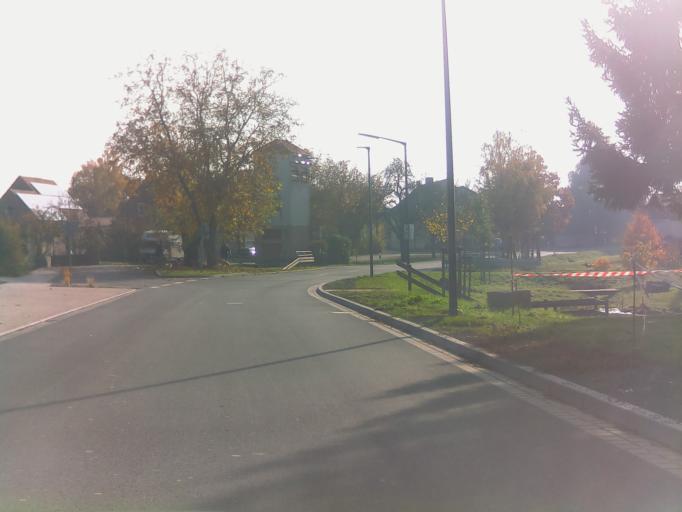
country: DE
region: Bavaria
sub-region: Regierungsbezirk Unterfranken
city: Biebelried
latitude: 49.7633
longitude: 10.0794
